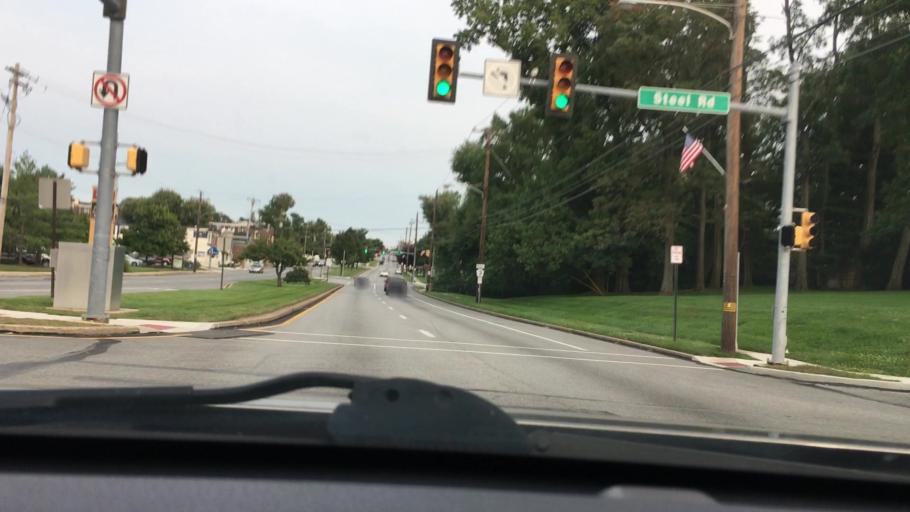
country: US
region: Pennsylvania
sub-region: Delaware County
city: Drexel Hill
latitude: 39.9703
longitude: -75.3042
